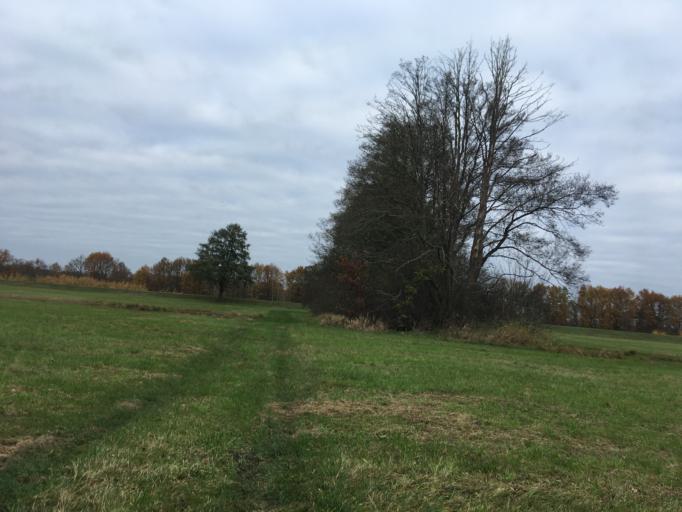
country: DE
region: Brandenburg
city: Werben
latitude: 51.8369
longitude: 14.1930
